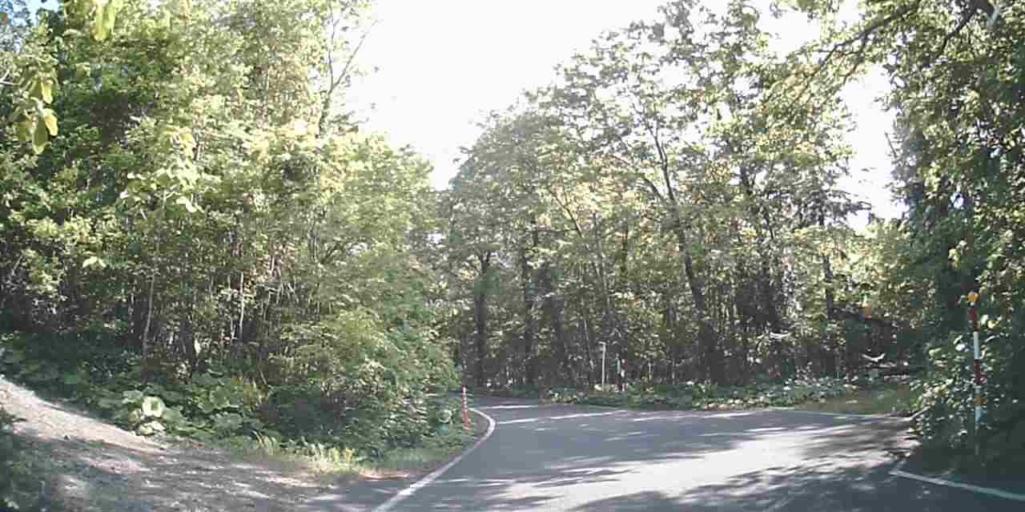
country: JP
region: Hokkaido
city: Shiraoi
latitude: 42.7229
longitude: 141.4121
